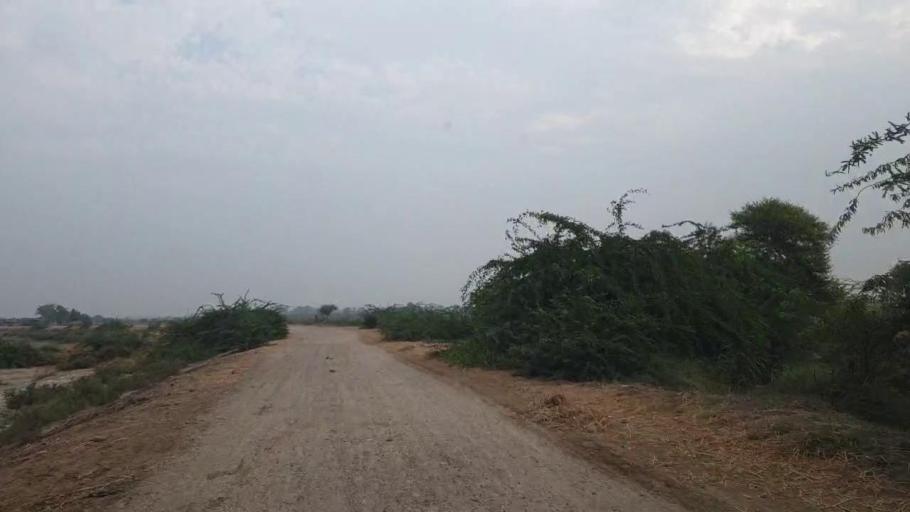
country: PK
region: Sindh
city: Talhar
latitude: 24.8104
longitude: 68.8747
